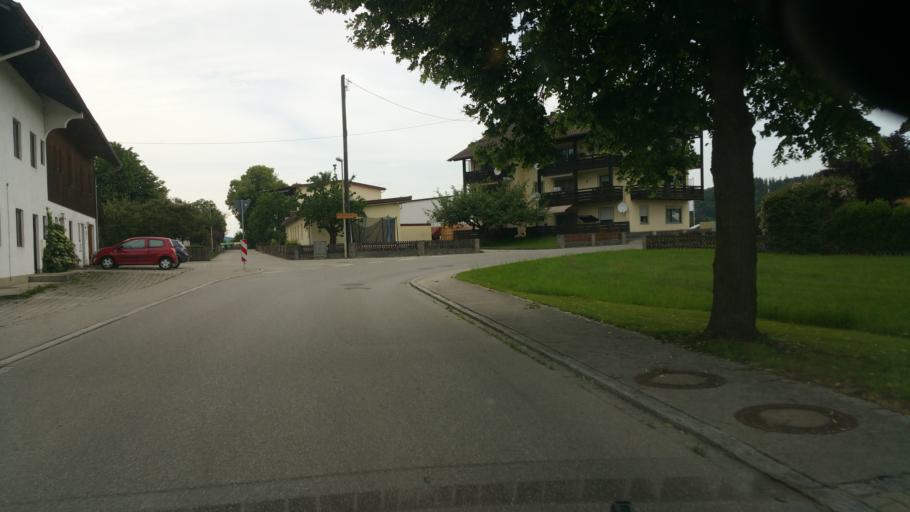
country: DE
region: Bavaria
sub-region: Upper Bavaria
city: Bruckmuhl
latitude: 47.8709
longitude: 11.9018
